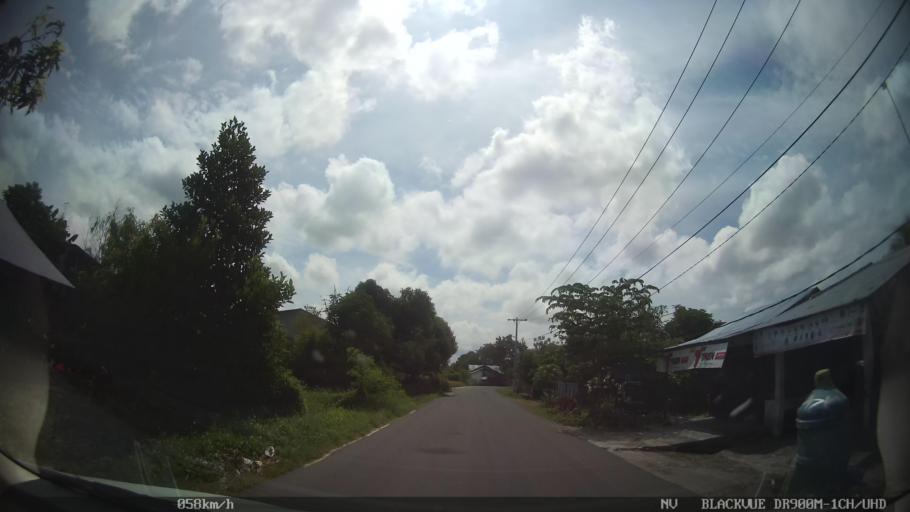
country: ID
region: North Sumatra
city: Percut
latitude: 3.5892
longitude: 98.8681
